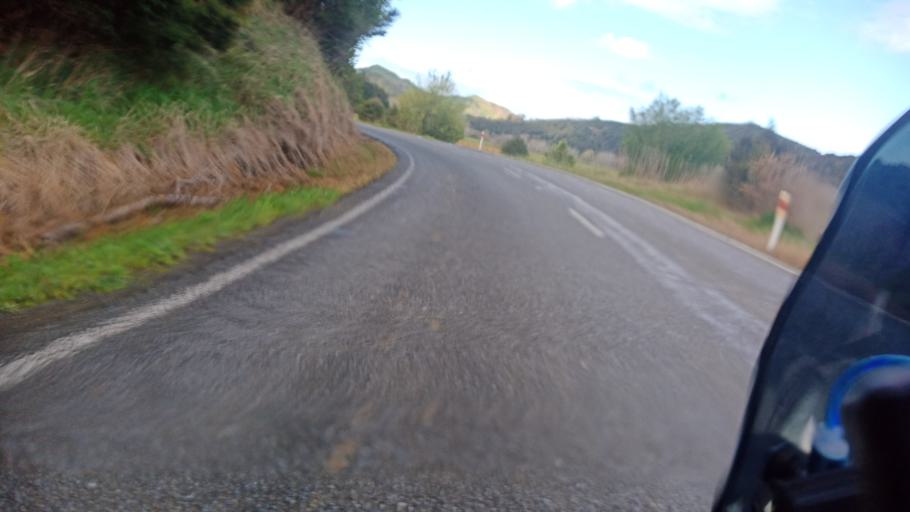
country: NZ
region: Gisborne
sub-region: Gisborne District
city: Gisborne
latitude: -38.2978
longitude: 178.2631
